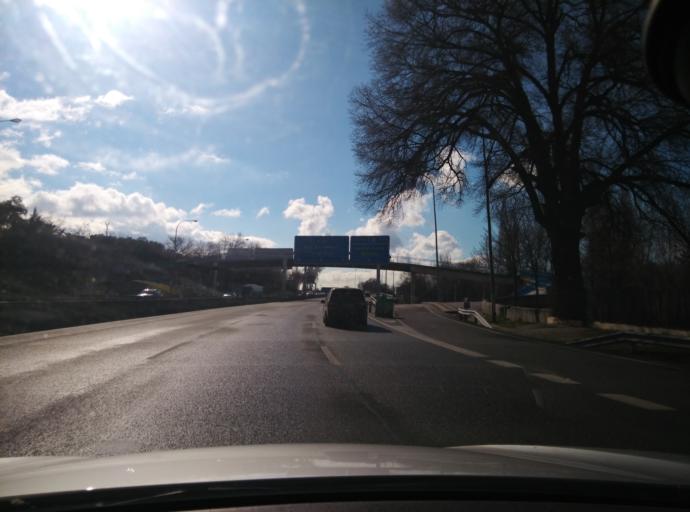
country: ES
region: Madrid
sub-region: Provincia de Madrid
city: Moncloa-Aravaca
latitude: 40.4605
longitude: -3.7458
